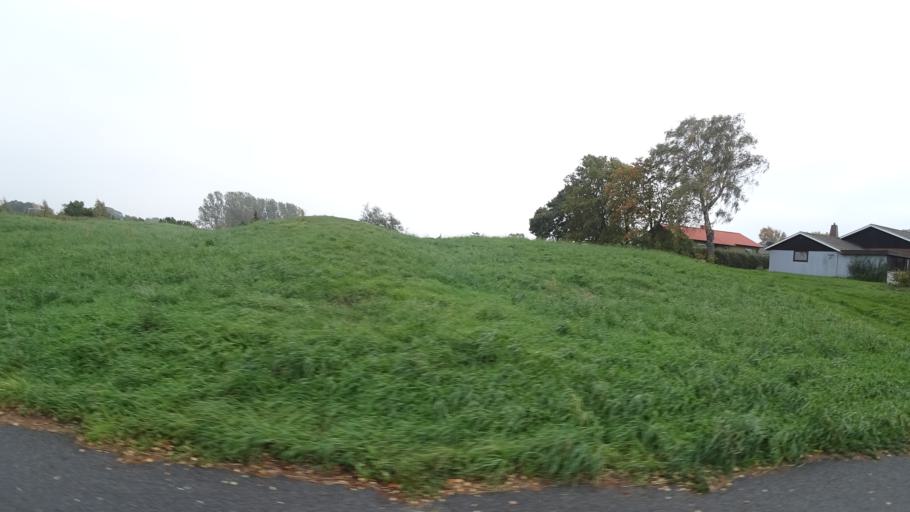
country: SE
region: Skane
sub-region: Kavlinge Kommun
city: Loddekopinge
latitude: 55.7566
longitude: 13.0126
